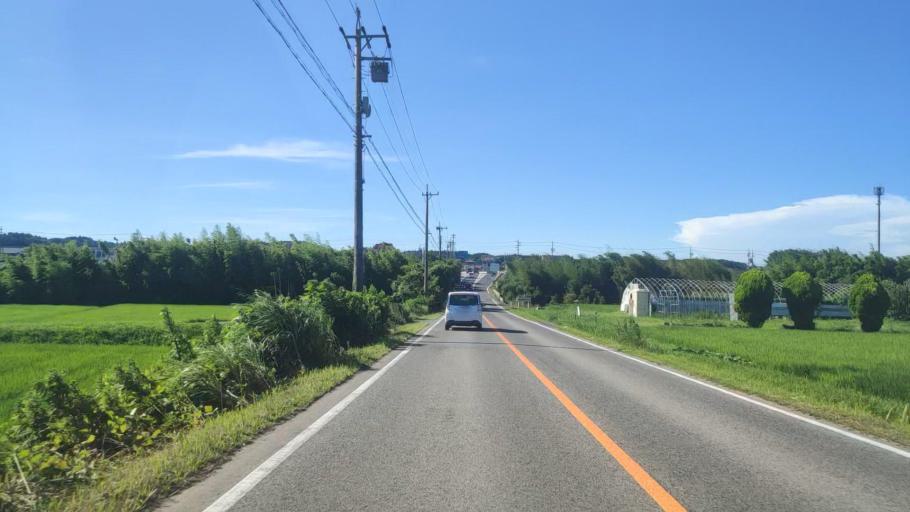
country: JP
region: Mie
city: Ueno-ebisumachi
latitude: 34.8345
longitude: 136.2361
